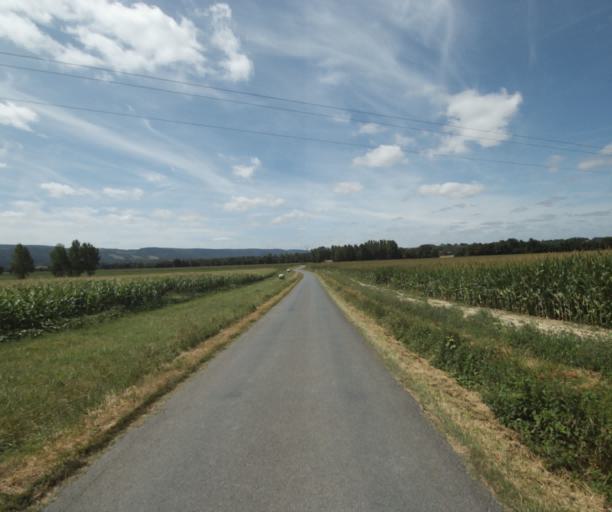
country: FR
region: Midi-Pyrenees
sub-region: Departement du Tarn
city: Dourgne
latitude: 43.5024
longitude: 2.0899
